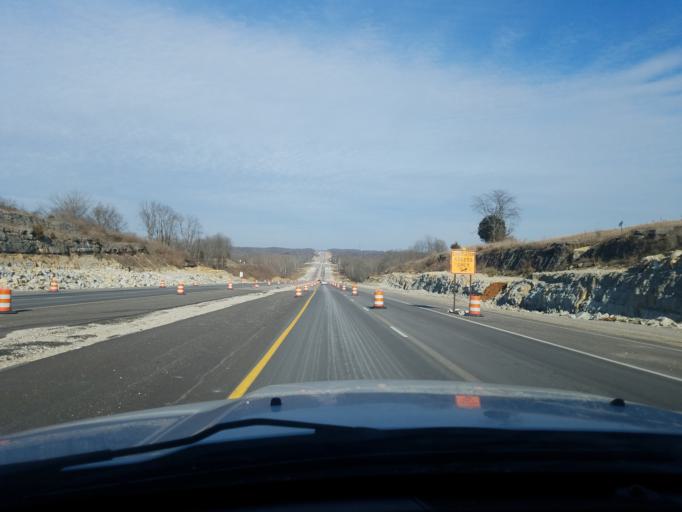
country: US
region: Indiana
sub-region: Monroe County
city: Bloomington
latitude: 39.2234
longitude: -86.5484
